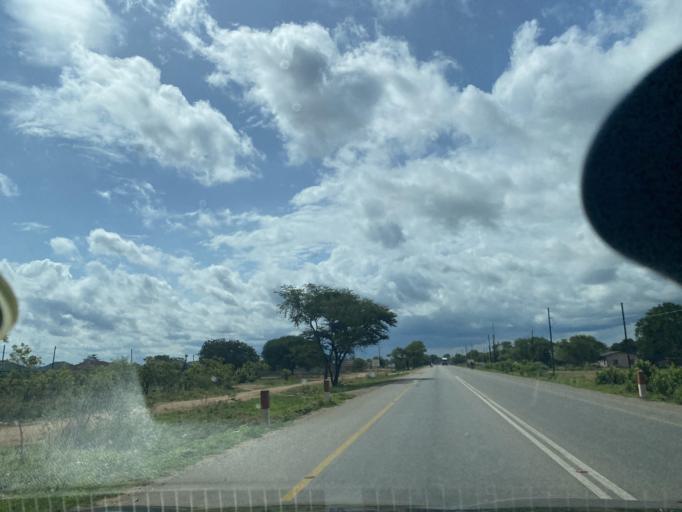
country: ZM
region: Lusaka
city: Kafue
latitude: -15.8562
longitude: 28.2577
